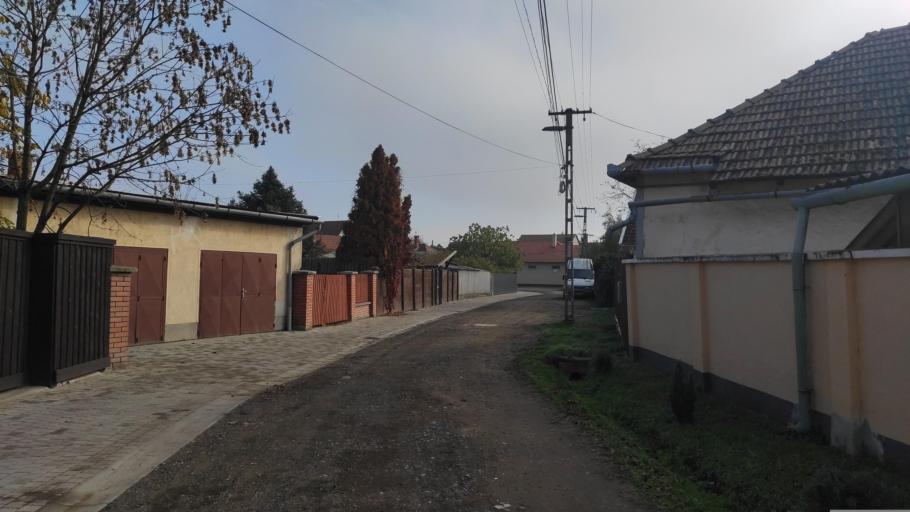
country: HU
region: Bekes
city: Bekes
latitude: 46.7668
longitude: 21.1358
